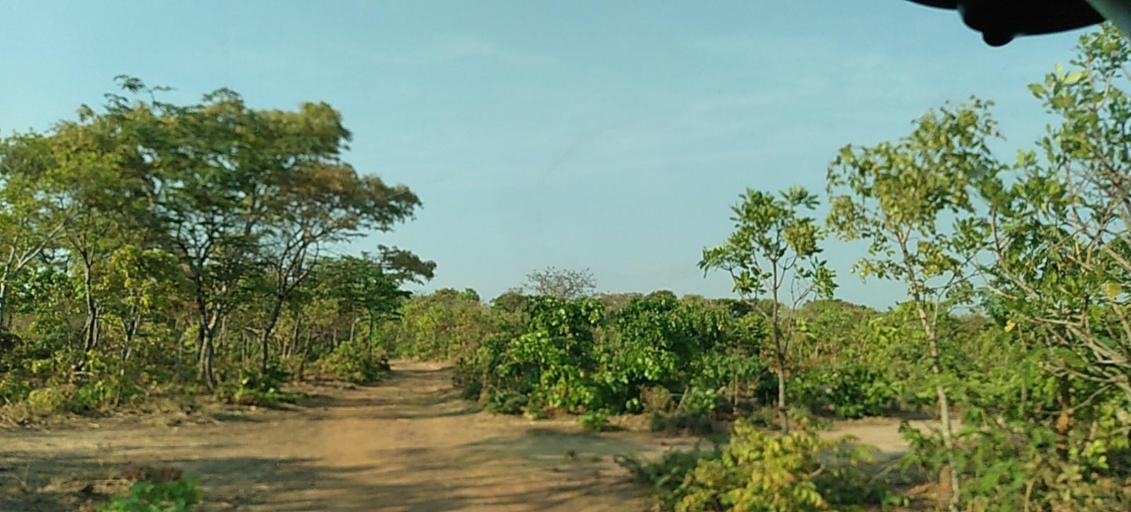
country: ZM
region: North-Western
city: Kalengwa
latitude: -13.1535
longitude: 25.0340
